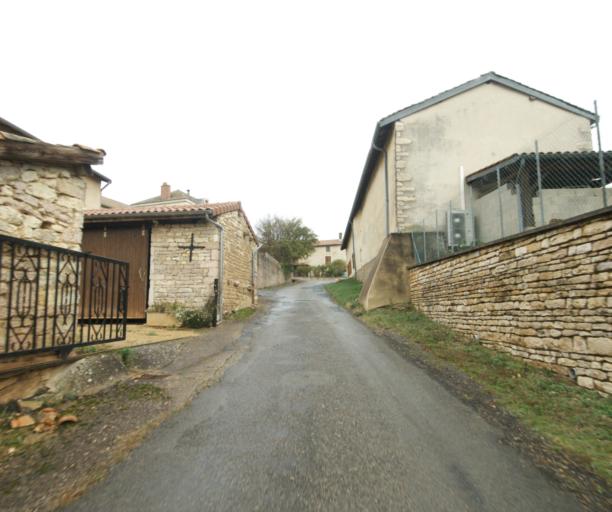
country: FR
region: Rhone-Alpes
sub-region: Departement de l'Ain
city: Pont-de-Vaux
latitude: 46.4753
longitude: 4.8727
